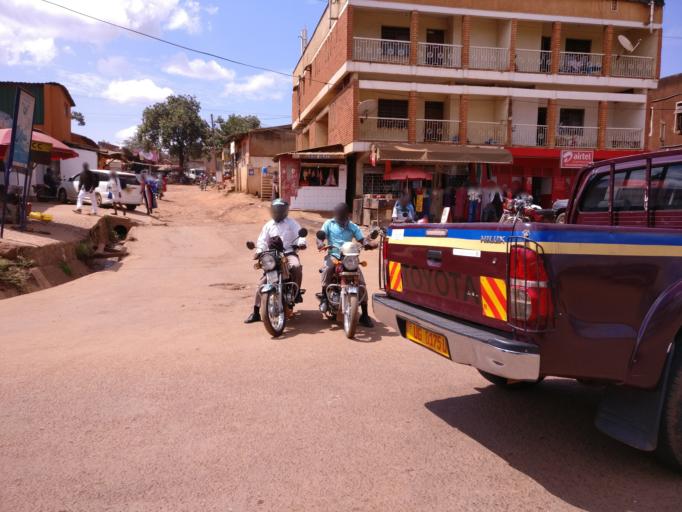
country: UG
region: Central Region
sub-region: Kampala District
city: Kampala
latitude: 0.2791
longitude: 32.5660
